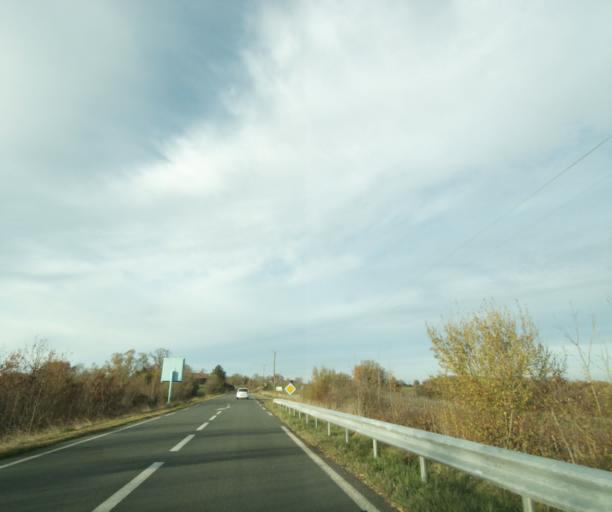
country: FR
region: Midi-Pyrenees
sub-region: Departement du Gers
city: Eauze
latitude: 43.7943
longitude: 0.1002
